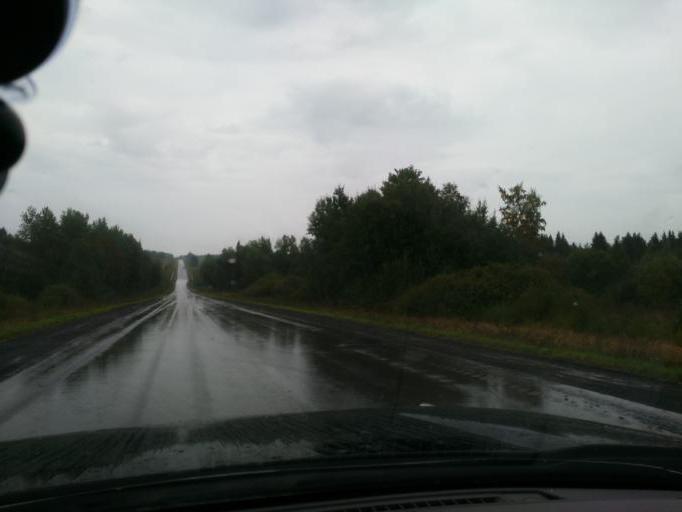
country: RU
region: Perm
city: Yugo-Kamskiy
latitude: 57.4813
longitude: 55.6806
